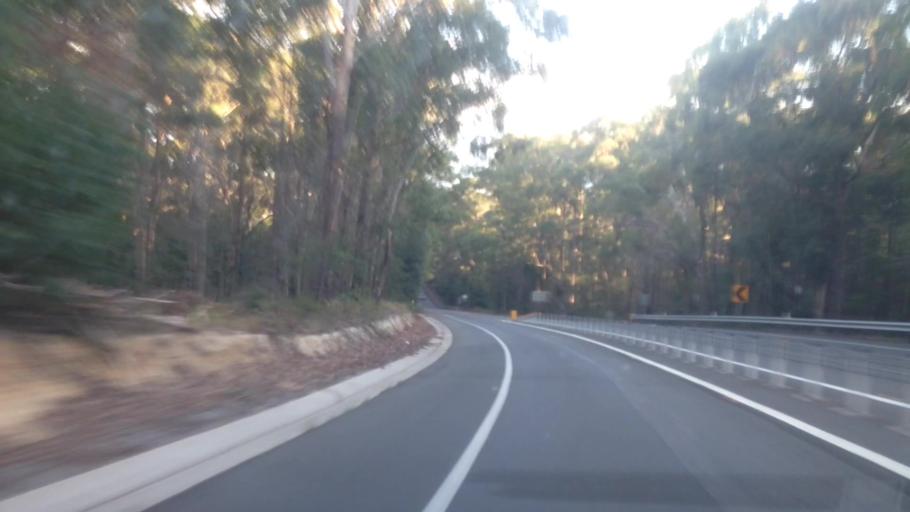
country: AU
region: New South Wales
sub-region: Lake Macquarie Shire
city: Cooranbong
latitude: -32.9743
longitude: 151.4820
